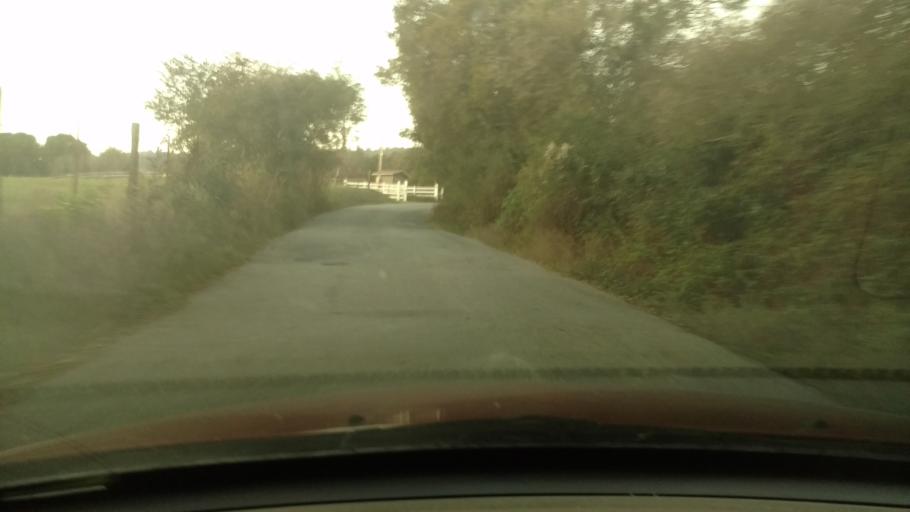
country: US
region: California
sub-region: Santa Cruz County
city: Interlaken
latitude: 36.9955
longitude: -121.7341
